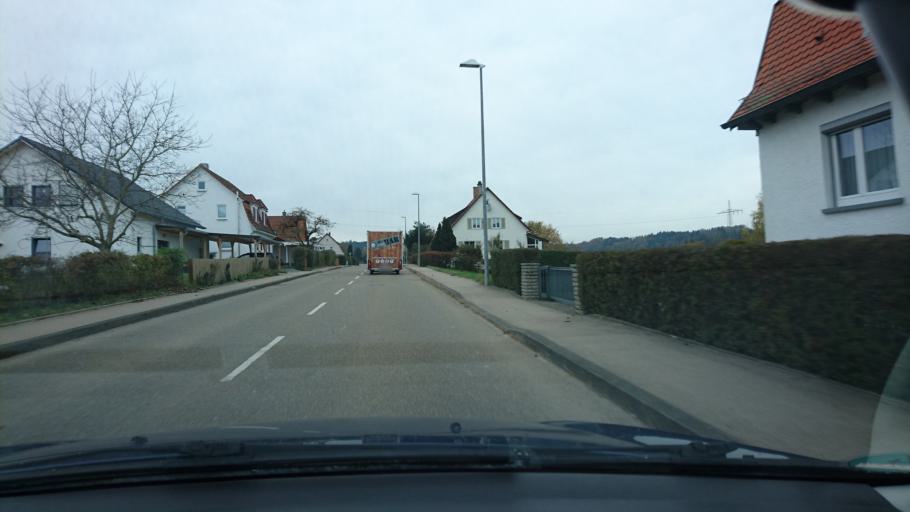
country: DE
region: Baden-Wuerttemberg
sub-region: Regierungsbezirk Stuttgart
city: Gschwend
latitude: 48.9348
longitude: 9.7372
